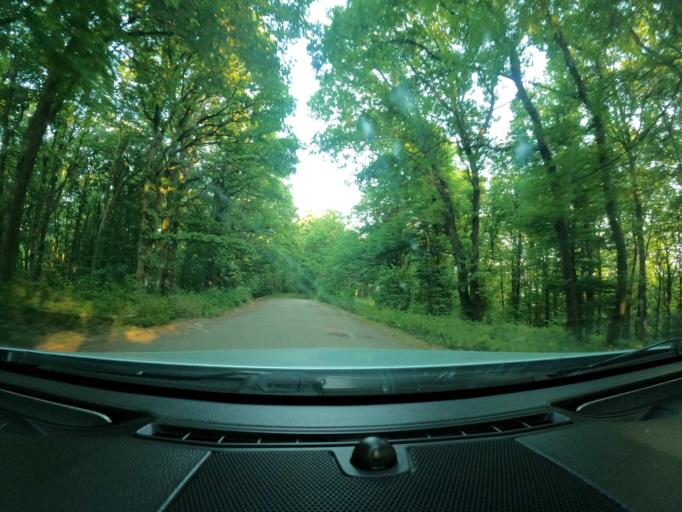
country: RS
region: Autonomna Pokrajina Vojvodina
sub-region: Juznobacki Okrug
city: Beocin
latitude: 45.1540
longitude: 19.7254
